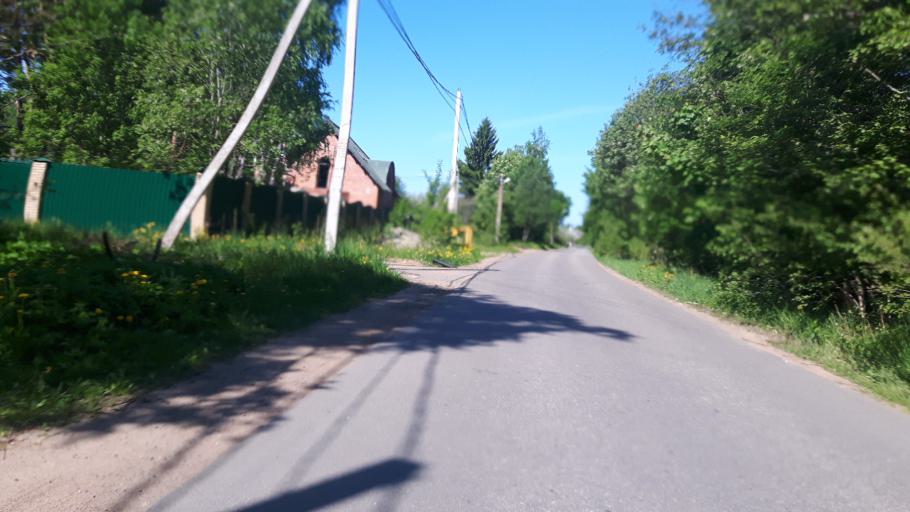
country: RU
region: Leningrad
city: Lebyazh'ye
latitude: 59.9707
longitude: 29.3852
